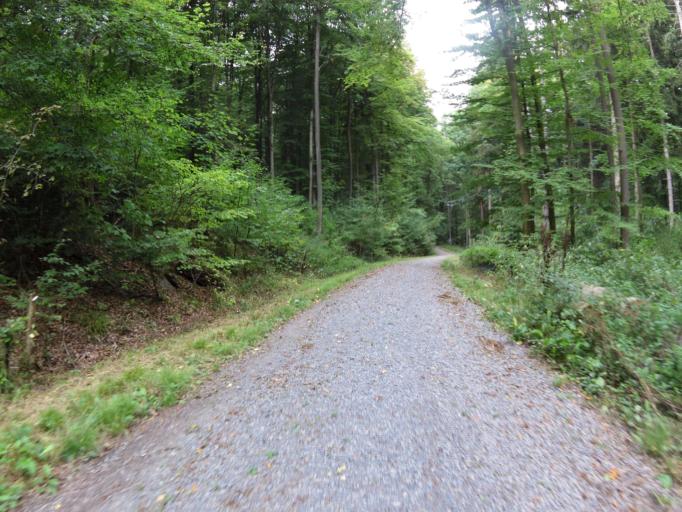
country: DE
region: Bavaria
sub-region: Regierungsbezirk Unterfranken
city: Waldbrunn
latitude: 49.7699
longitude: 9.7966
